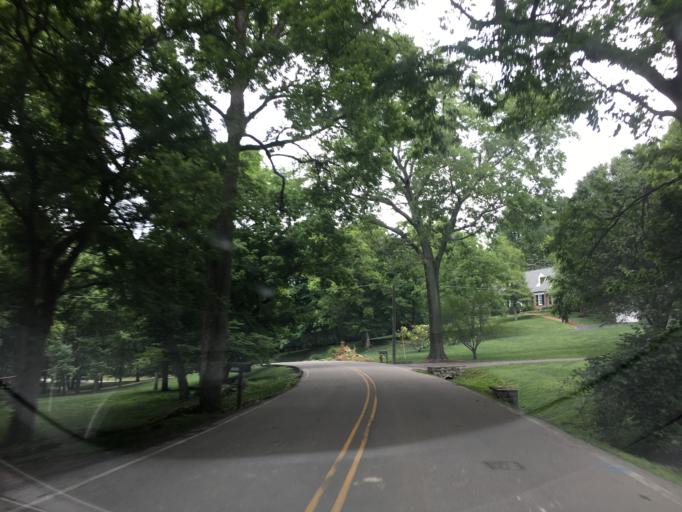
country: US
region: Tennessee
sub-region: Davidson County
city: Forest Hills
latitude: 36.0876
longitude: -86.8274
